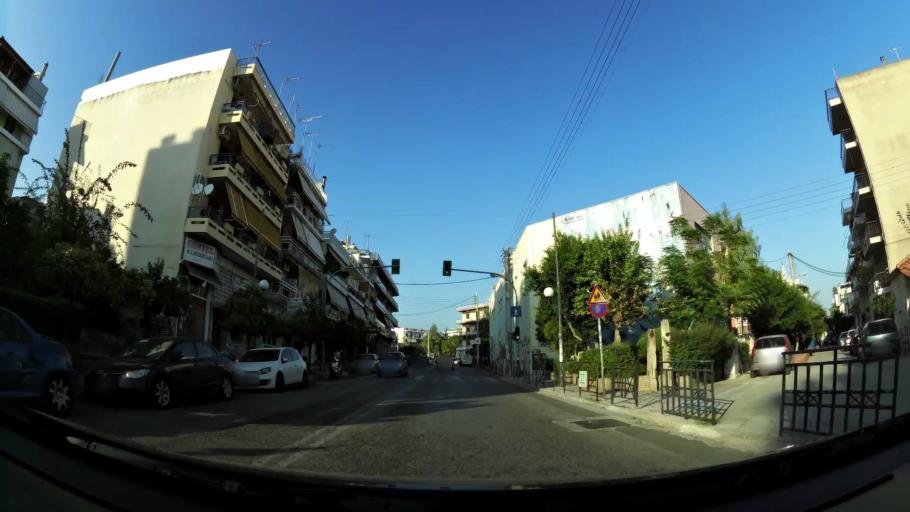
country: GR
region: Attica
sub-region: Nomos Piraios
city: Korydallos
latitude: 37.9744
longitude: 23.6405
